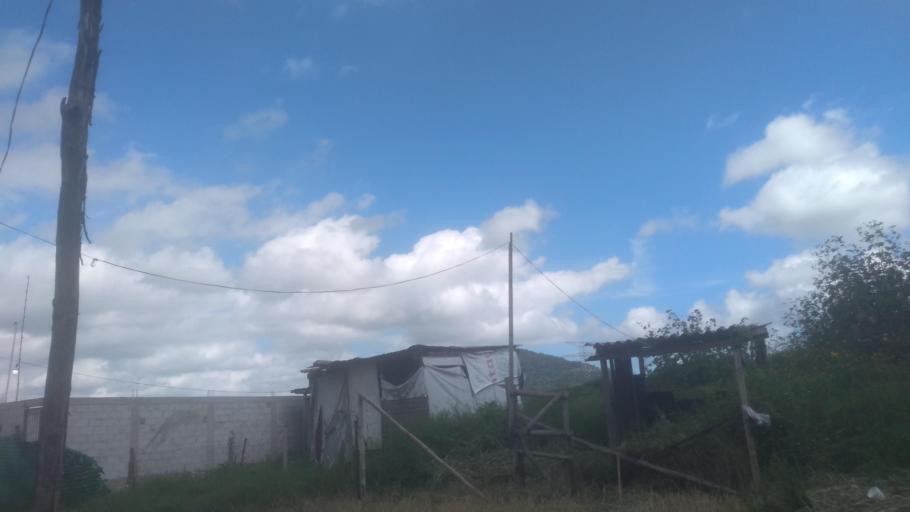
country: MX
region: Veracruz
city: Ixtac Zoquitlan
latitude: 18.8801
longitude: -97.0630
